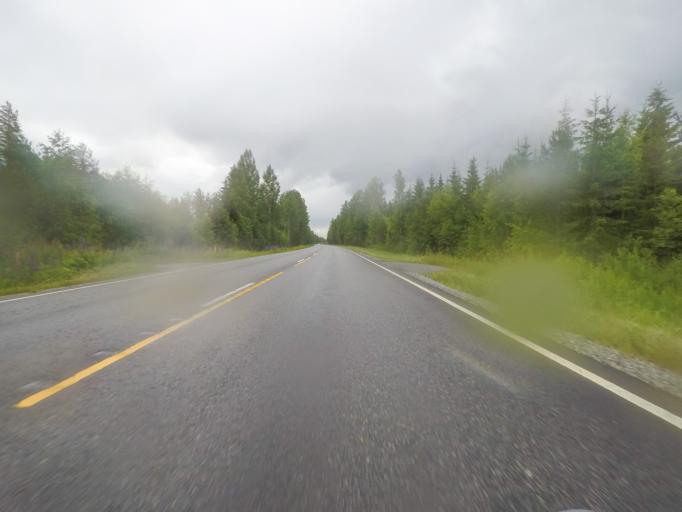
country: FI
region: Central Finland
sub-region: Jyvaeskylae
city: Toivakka
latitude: 62.2196
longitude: 26.2036
